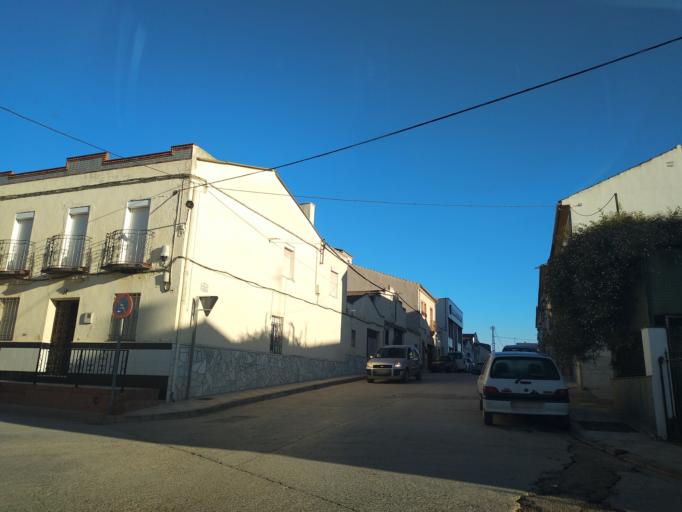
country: ES
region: Andalusia
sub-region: Provincia de Malaga
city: Campillos
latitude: 37.0513
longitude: -4.8660
